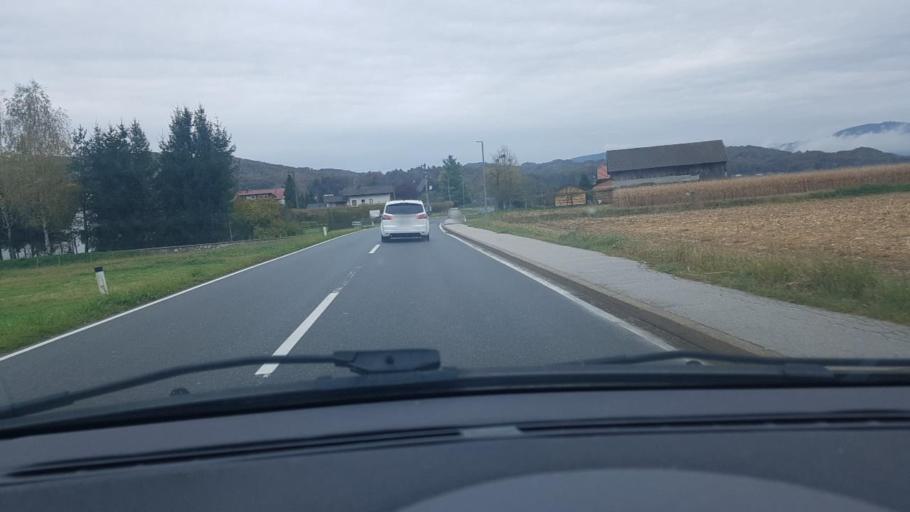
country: SI
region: Majsperk
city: Majsperk
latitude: 46.3455
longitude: 15.7374
